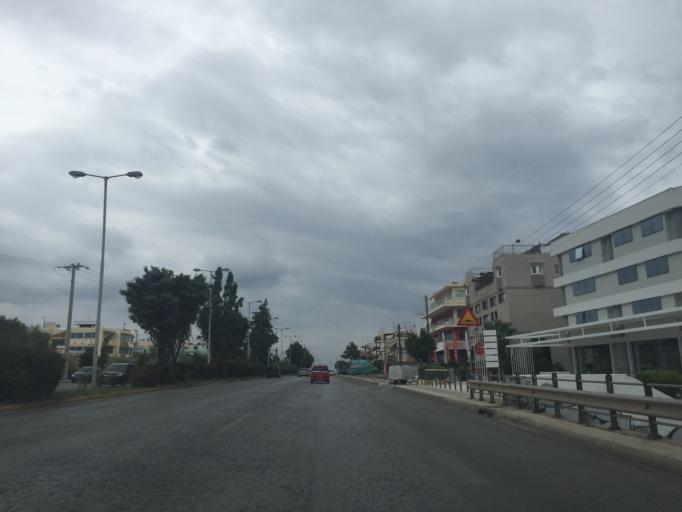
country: GR
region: Attica
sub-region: Nomarchia Athinas
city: Glyfada
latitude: 37.8531
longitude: 23.7671
